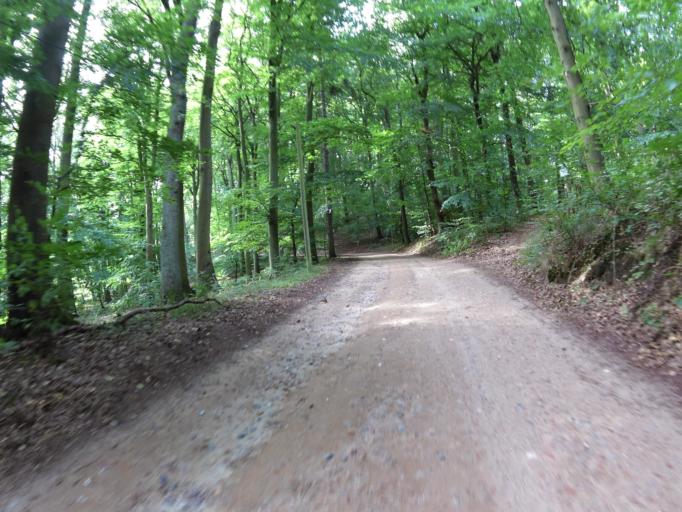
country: DE
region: Mecklenburg-Vorpommern
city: Seebad Bansin
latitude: 53.9620
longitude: 14.1078
